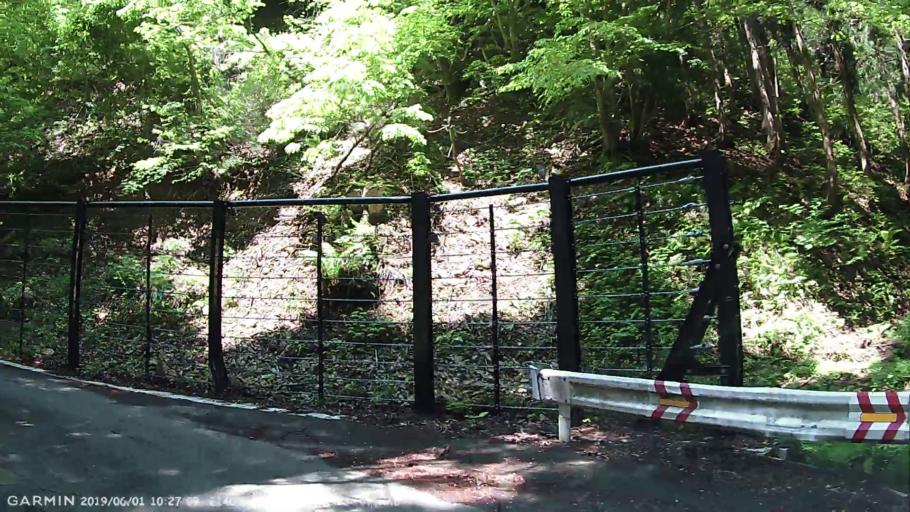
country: JP
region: Fukushima
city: Inawashiro
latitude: 37.3292
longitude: 140.0837
